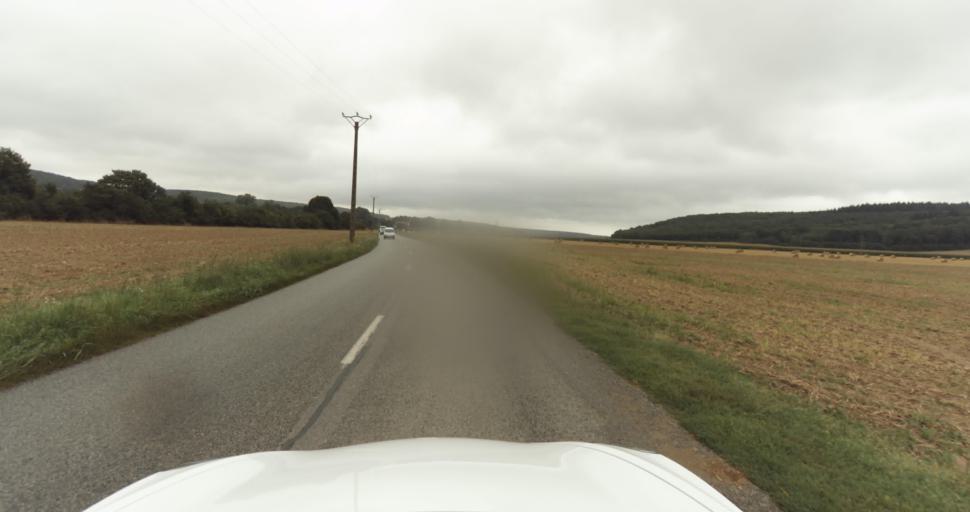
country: FR
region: Haute-Normandie
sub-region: Departement de l'Eure
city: Normanville
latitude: 49.0795
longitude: 1.1438
